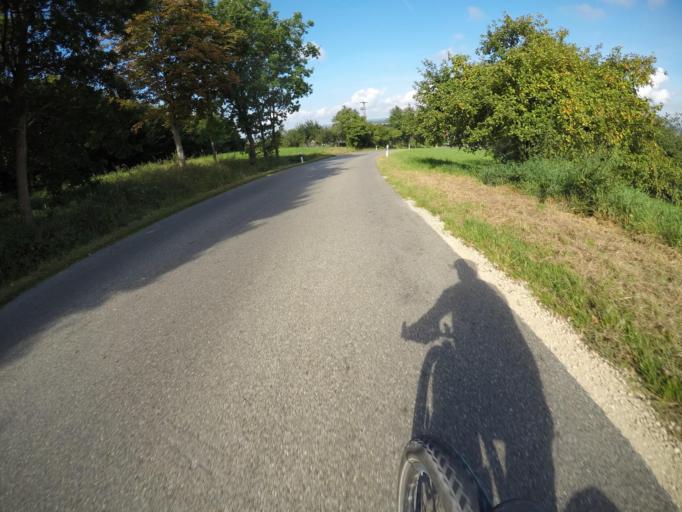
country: DE
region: Bavaria
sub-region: Swabia
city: Buttenwiesen
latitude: 48.6233
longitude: 10.7520
